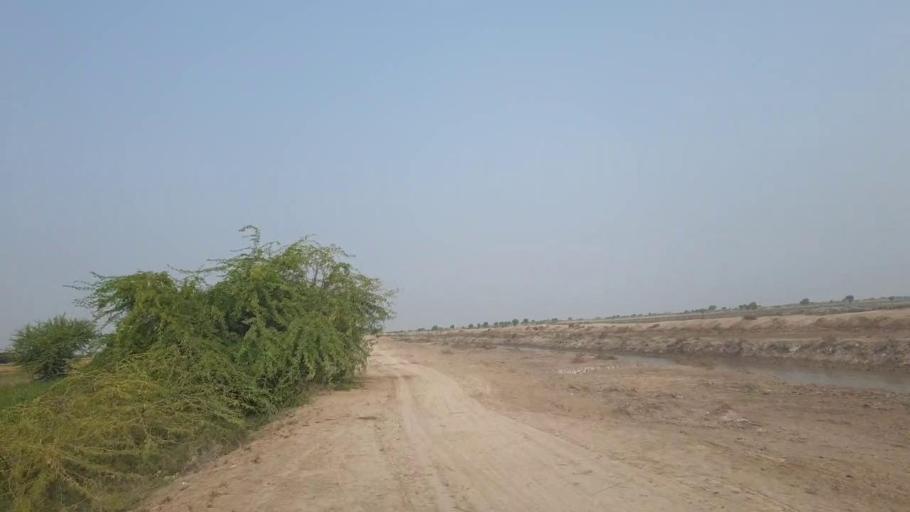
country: PK
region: Sindh
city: Badin
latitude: 24.7206
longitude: 68.7703
